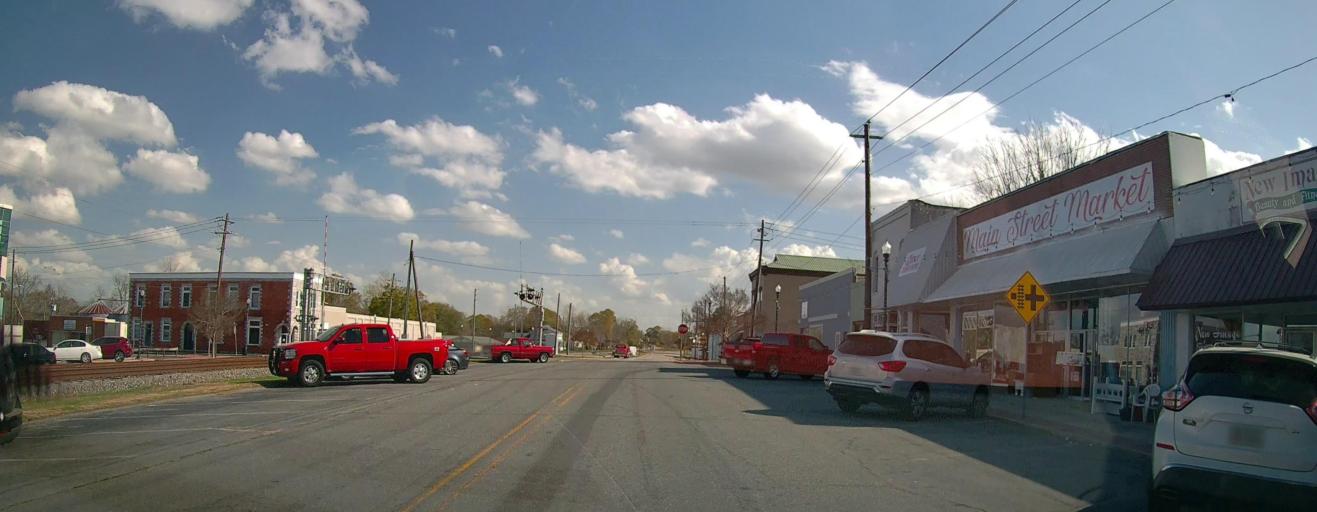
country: US
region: Georgia
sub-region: Dodge County
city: Eastman
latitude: 32.1975
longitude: -83.1759
